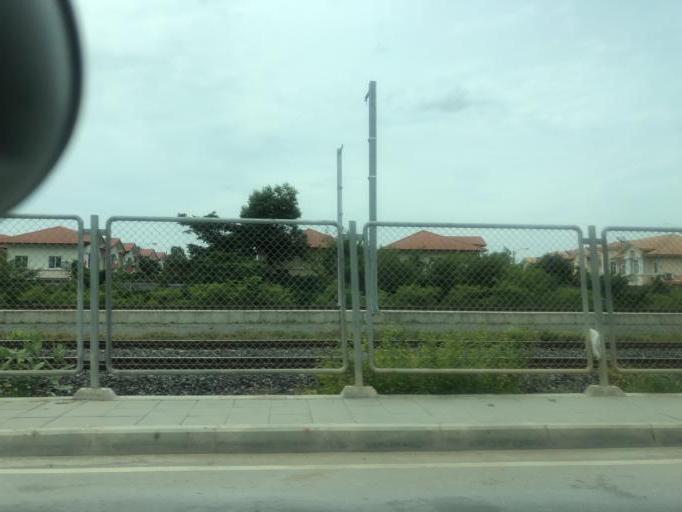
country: TH
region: Bangkok
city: Don Mueang
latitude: 13.9502
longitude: 100.6070
